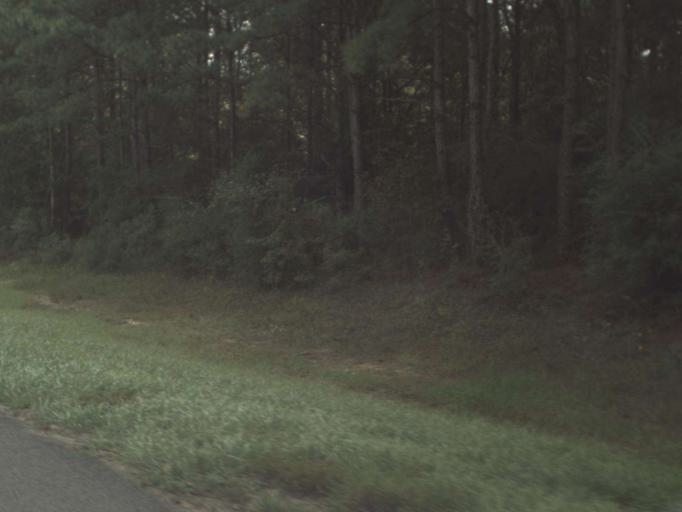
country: US
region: Florida
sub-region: Walton County
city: Freeport
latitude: 30.5547
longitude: -85.9165
